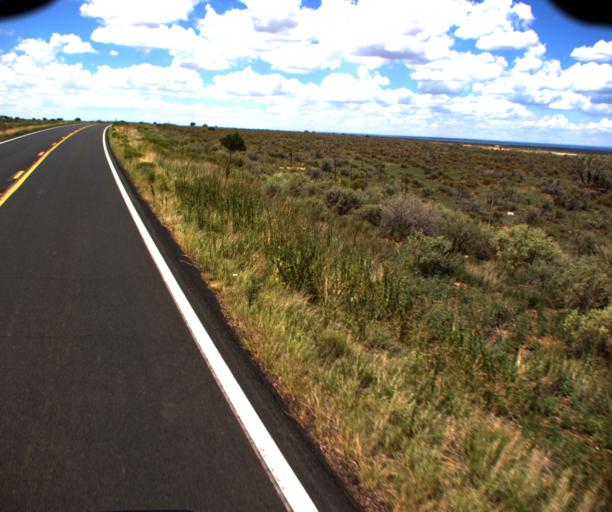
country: US
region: Arizona
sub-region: Coconino County
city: Williams
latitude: 35.6244
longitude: -112.1112
